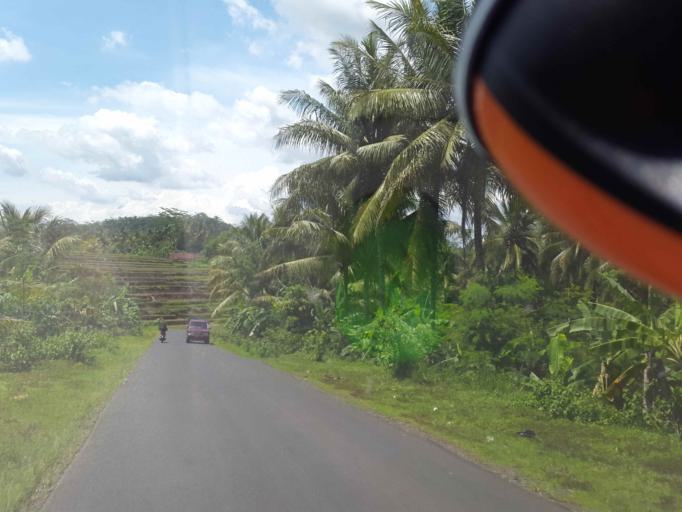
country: ID
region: Central Java
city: Purbalingga
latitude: -7.3859
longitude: 109.5943
